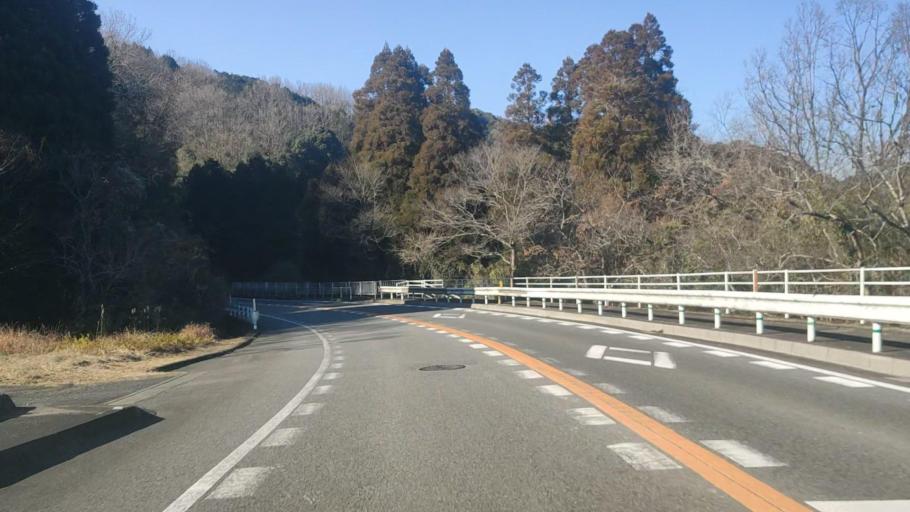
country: JP
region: Oita
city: Usuki
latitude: 33.0217
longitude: 131.6963
